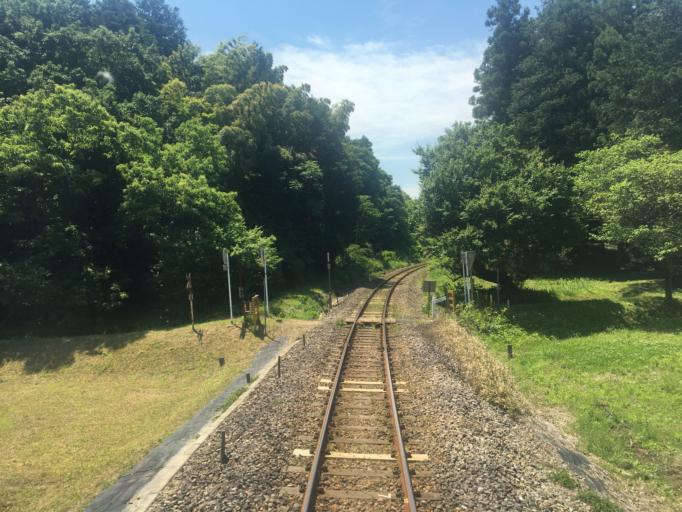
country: JP
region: Saitama
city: Ogawa
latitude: 36.0479
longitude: 139.2660
